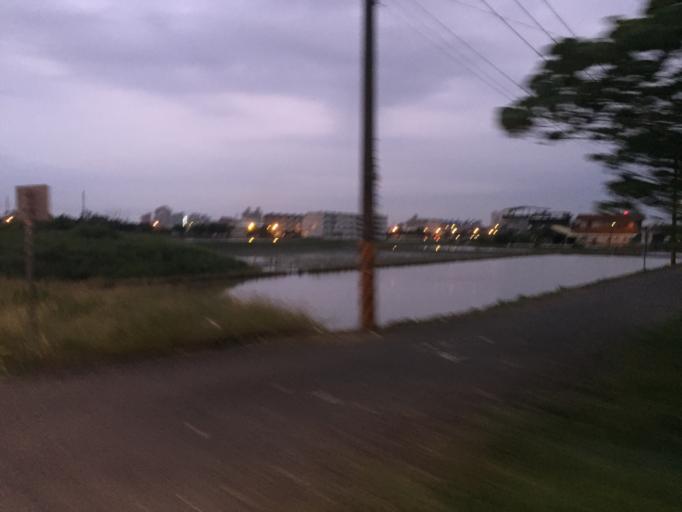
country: TW
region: Taiwan
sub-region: Yilan
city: Yilan
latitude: 24.7670
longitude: 121.7400
